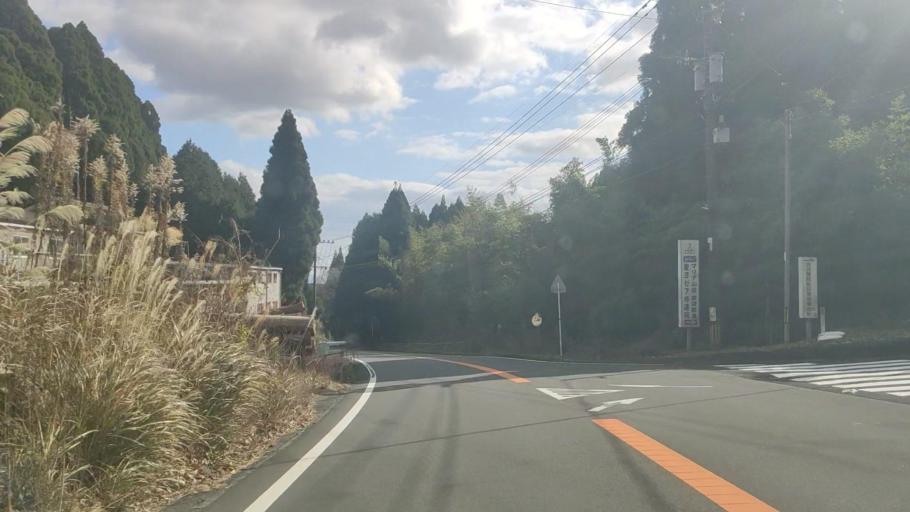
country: JP
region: Kagoshima
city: Kajiki
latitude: 31.8265
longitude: 130.6891
